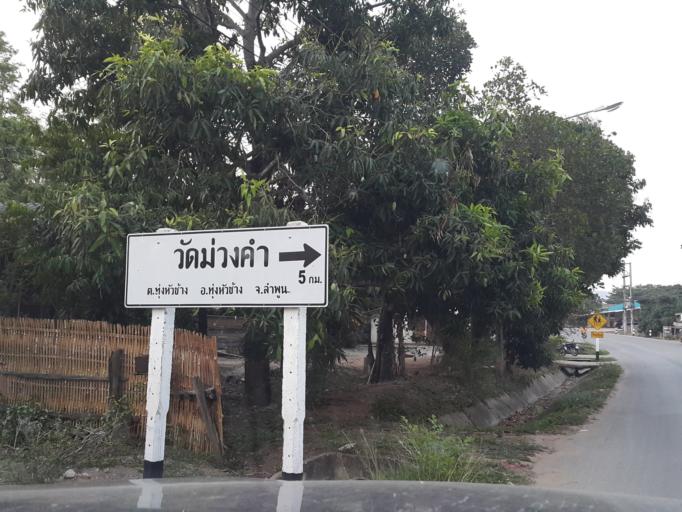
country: TH
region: Lamphun
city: Thung Hua Chang
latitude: 17.9961
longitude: 99.0312
